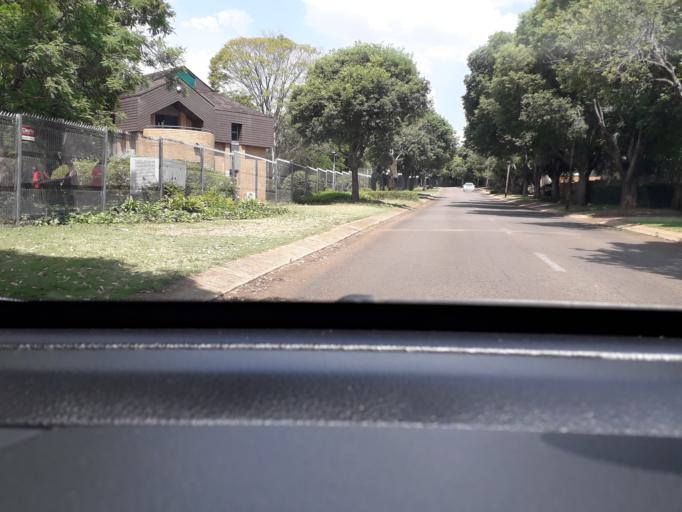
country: ZA
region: Gauteng
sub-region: City of Tshwane Metropolitan Municipality
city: Pretoria
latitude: -25.7720
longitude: 28.2126
